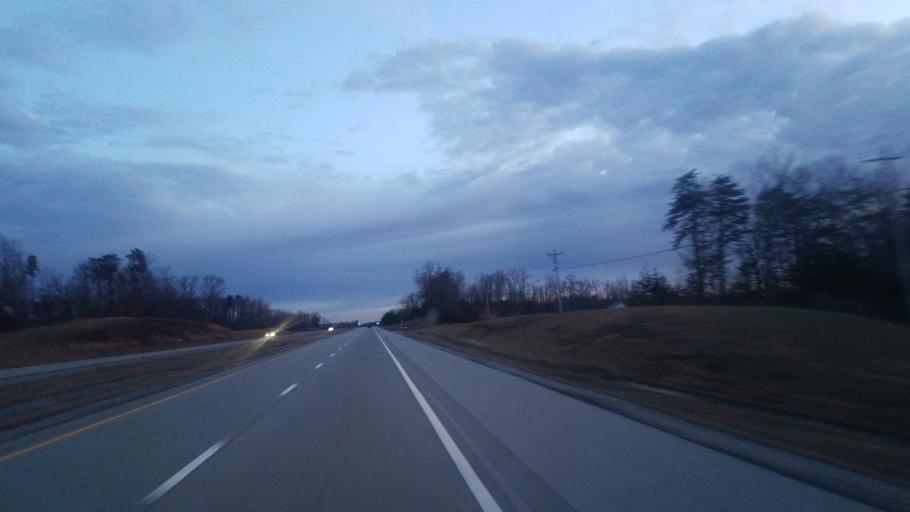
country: US
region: Tennessee
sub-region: Van Buren County
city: Spencer
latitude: 35.7064
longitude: -85.4759
